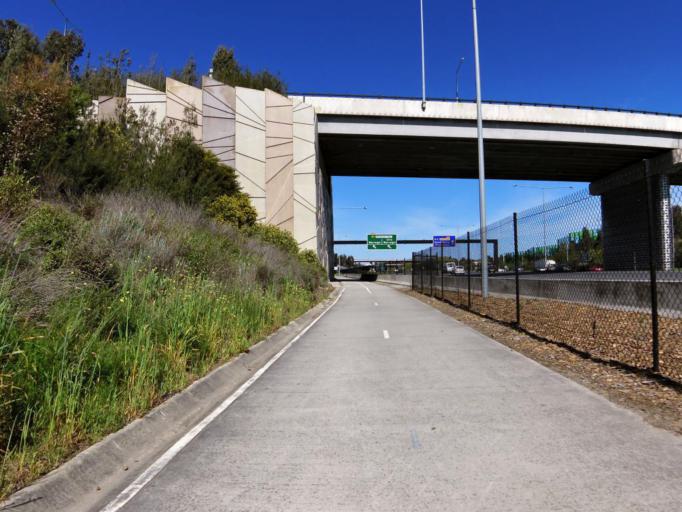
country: AU
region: Victoria
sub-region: Greater Dandenong
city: Noble Park North
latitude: -37.9385
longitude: 145.2077
